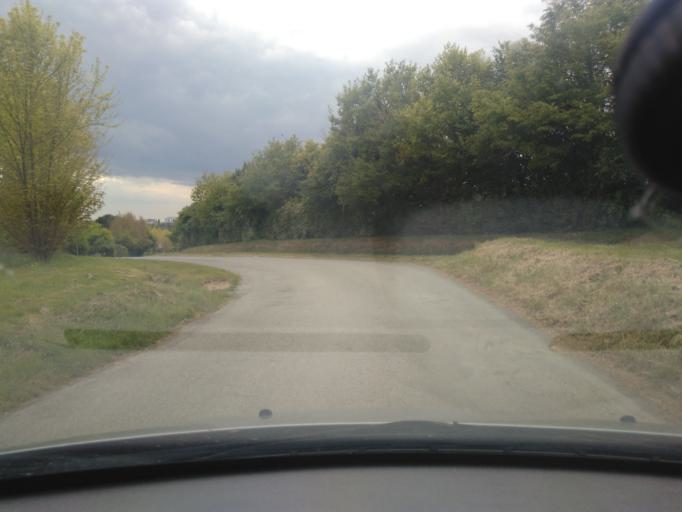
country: FR
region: Pays de la Loire
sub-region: Departement de la Vendee
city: La Roche-sur-Yon
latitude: 46.6947
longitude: -1.4135
